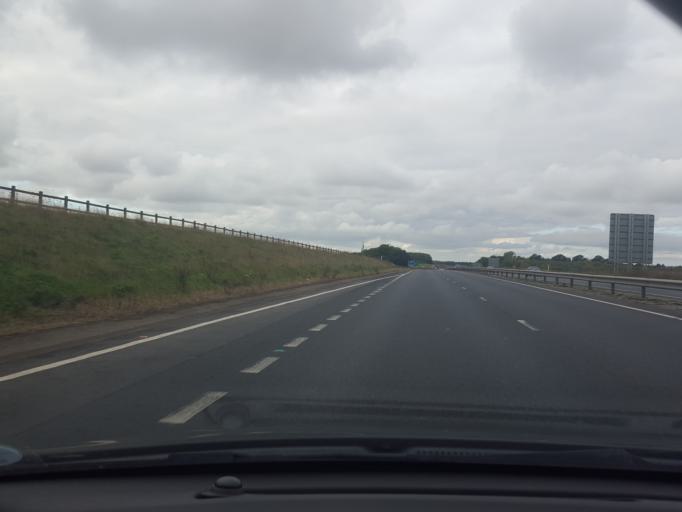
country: GB
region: England
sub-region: Suffolk
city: Stowmarket
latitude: 52.2083
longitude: 0.9695
